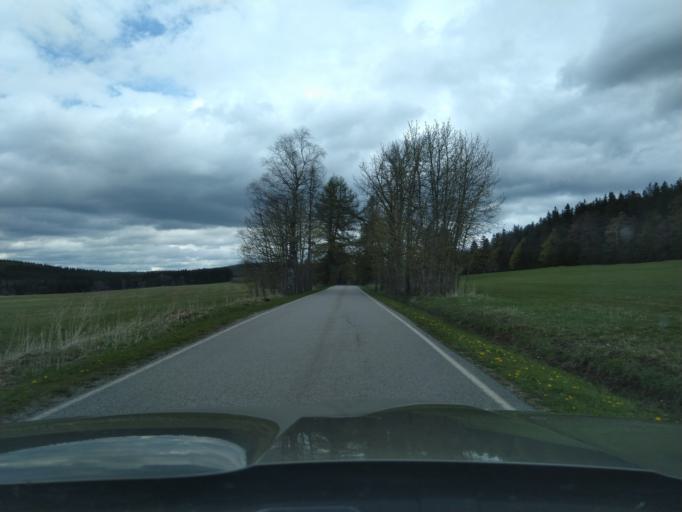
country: CZ
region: Jihocesky
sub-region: Okres Prachatice
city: Borova Lada
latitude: 49.0362
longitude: 13.6675
